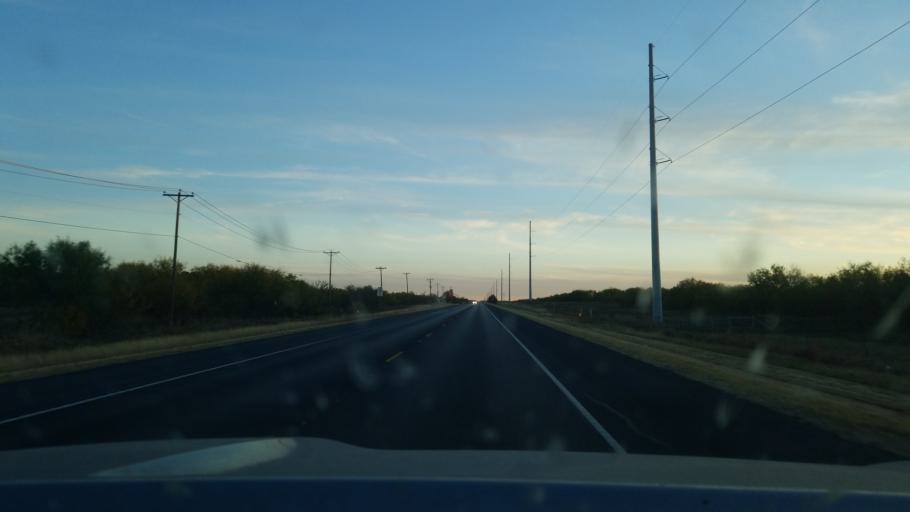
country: US
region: Texas
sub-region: Stephens County
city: Breckenridge
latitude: 32.7263
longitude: -98.9025
